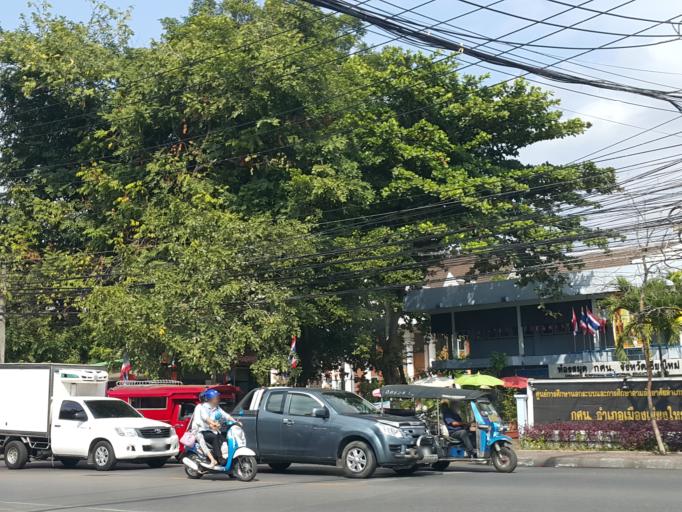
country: TH
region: Chiang Mai
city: Chiang Mai
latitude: 18.7959
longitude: 98.9782
